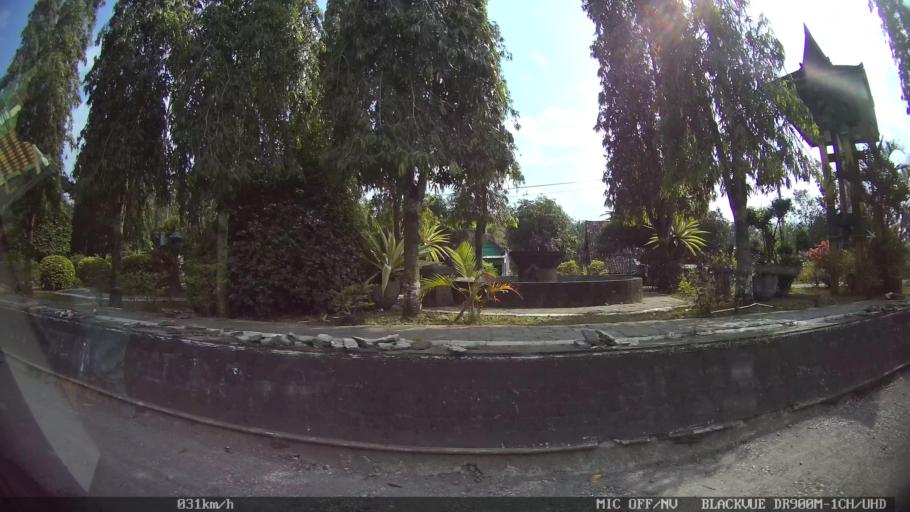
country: ID
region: Daerah Istimewa Yogyakarta
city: Srandakan
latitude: -7.8687
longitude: 110.1914
